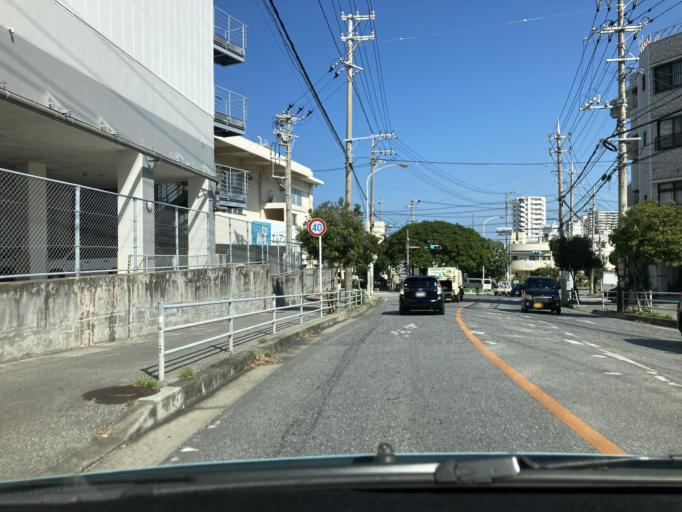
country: JP
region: Okinawa
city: Ginowan
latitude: 26.2608
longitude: 127.7227
